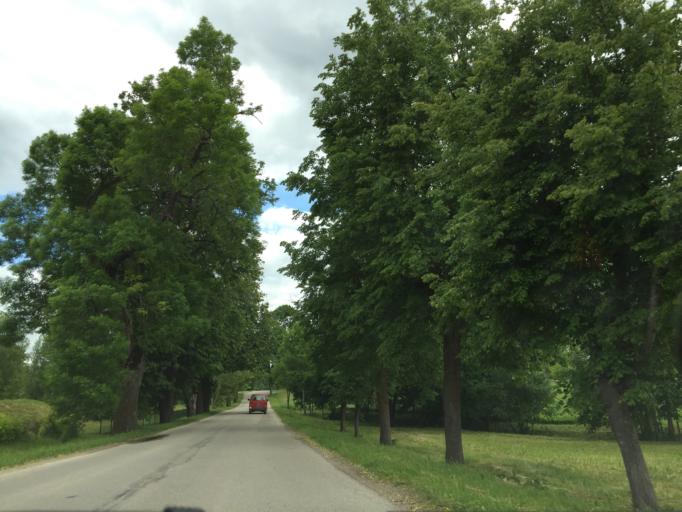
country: LV
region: Apes Novads
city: Ape
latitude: 57.5161
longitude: 26.4014
